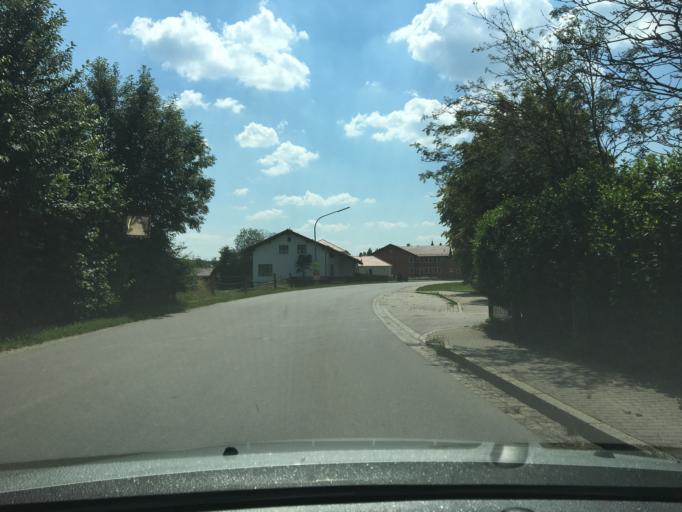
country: DE
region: Bavaria
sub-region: Lower Bavaria
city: Furth
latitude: 48.4273
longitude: 12.4161
